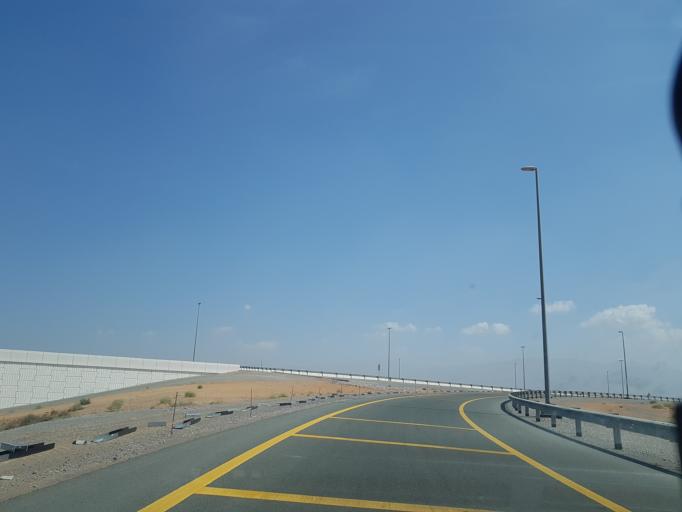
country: AE
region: Ra's al Khaymah
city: Ras al-Khaimah
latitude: 25.6942
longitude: 55.9247
